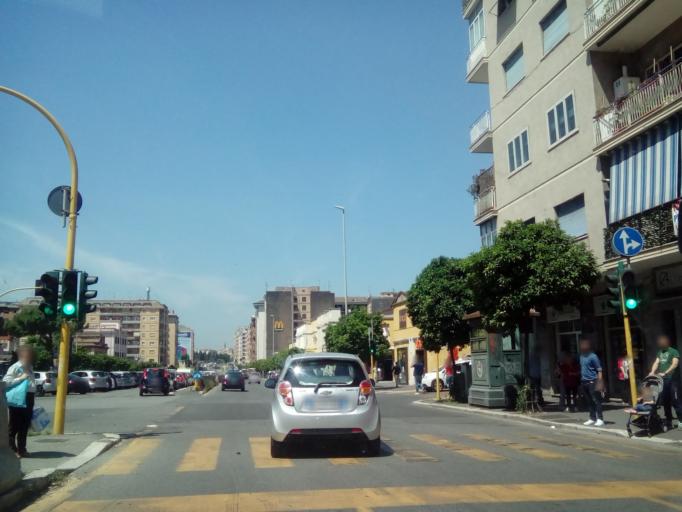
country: IT
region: Latium
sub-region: Citta metropolitana di Roma Capitale
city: Rome
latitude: 41.9087
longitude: 12.5429
